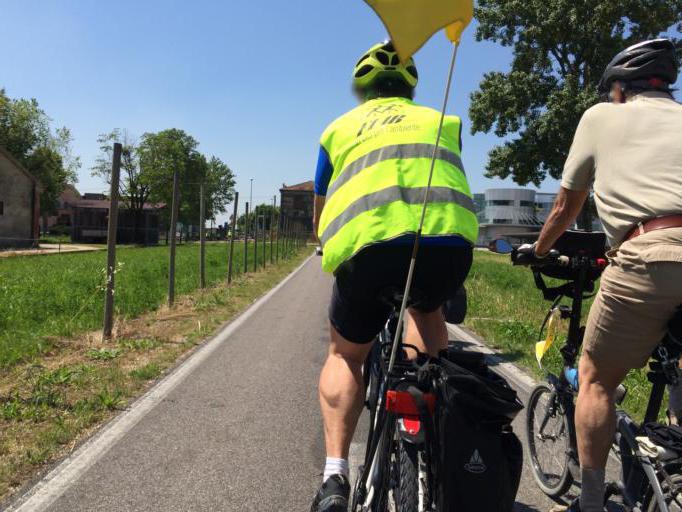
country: IT
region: Veneto
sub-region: Provincia di Vicenza
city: Ponte di Barbarano
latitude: 45.3974
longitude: 11.5665
